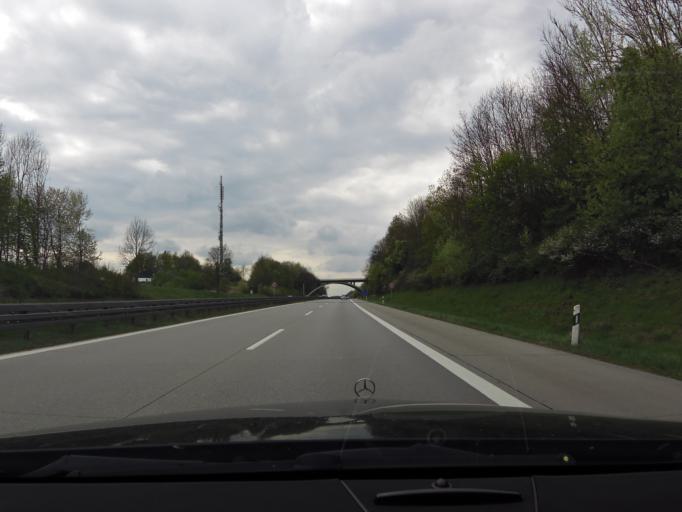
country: DE
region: Bavaria
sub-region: Lower Bavaria
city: Ergolding
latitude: 48.5702
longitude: 12.1163
